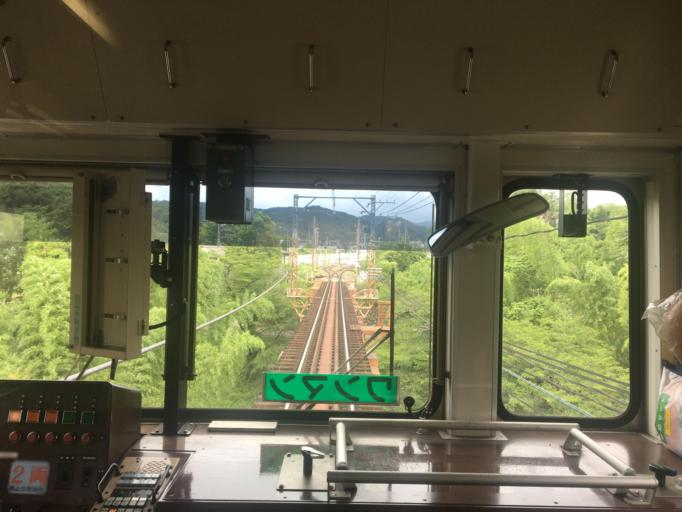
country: JP
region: Saitama
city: Yorii
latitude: 36.0843
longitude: 139.1142
